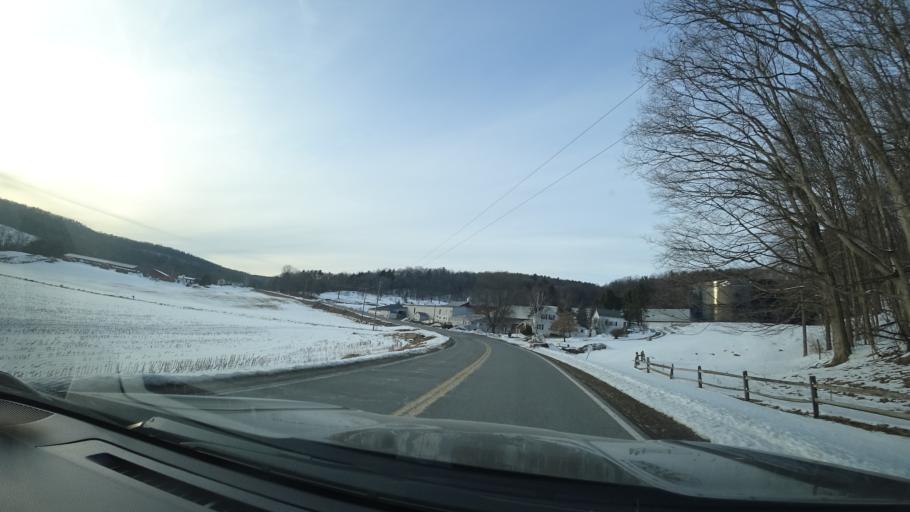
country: US
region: New York
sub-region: Washington County
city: Cambridge
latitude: 43.1881
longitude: -73.3712
